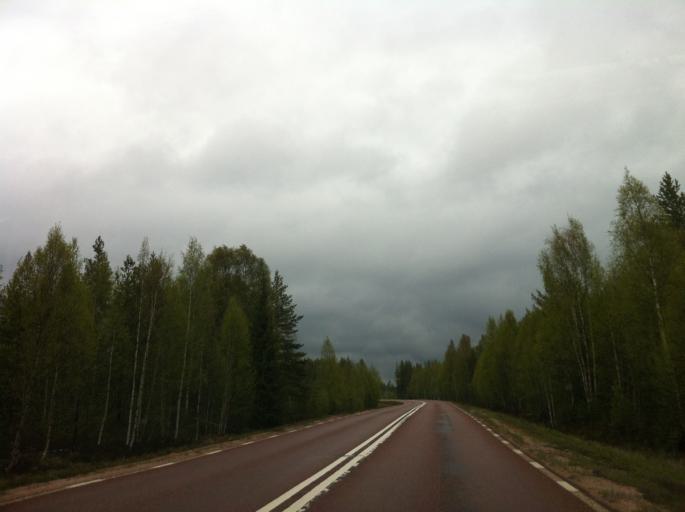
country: SE
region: Jaemtland
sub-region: Harjedalens Kommun
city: Sveg
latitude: 61.8934
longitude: 14.6223
